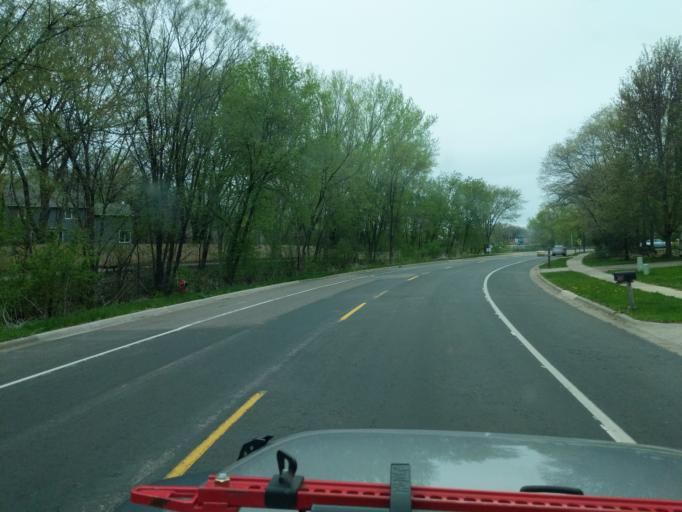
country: US
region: Minnesota
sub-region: Anoka County
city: Coon Rapids
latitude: 45.1524
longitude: -93.3084
